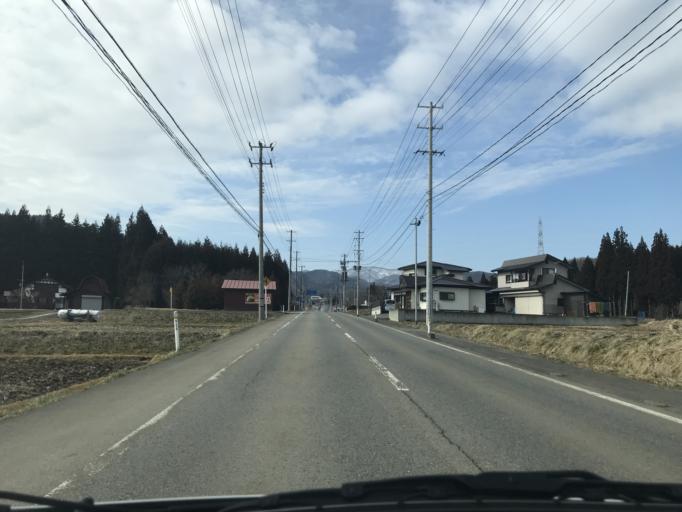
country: JP
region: Iwate
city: Hanamaki
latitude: 39.4004
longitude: 141.0313
